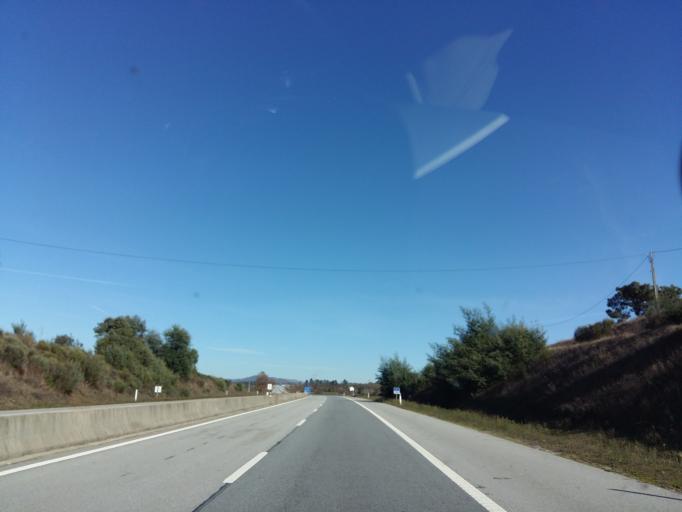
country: PT
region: Castelo Branco
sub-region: Covilha
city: Covilha
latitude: 40.2506
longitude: -7.4528
